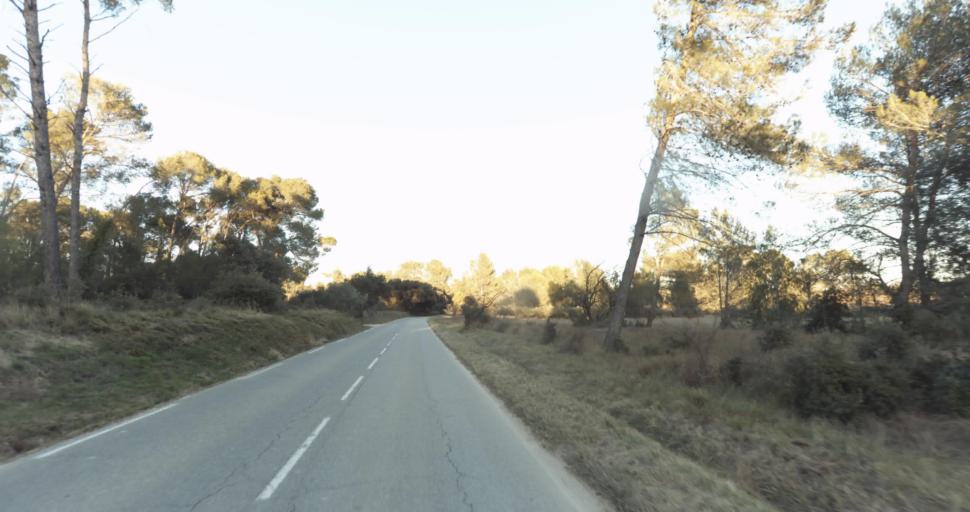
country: FR
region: Provence-Alpes-Cote d'Azur
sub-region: Departement des Bouches-du-Rhone
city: Barbentane
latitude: 43.8883
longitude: 4.7391
